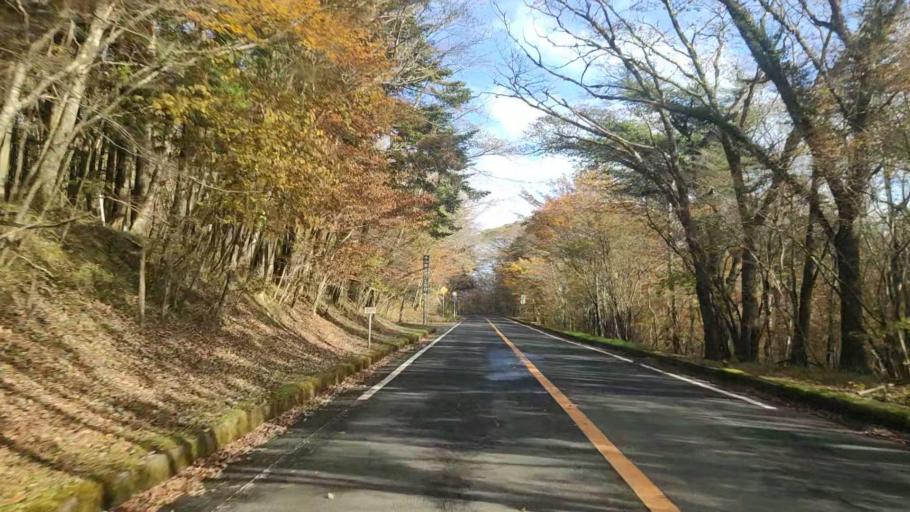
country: JP
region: Shizuoka
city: Fujinomiya
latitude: 35.2951
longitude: 138.7116
